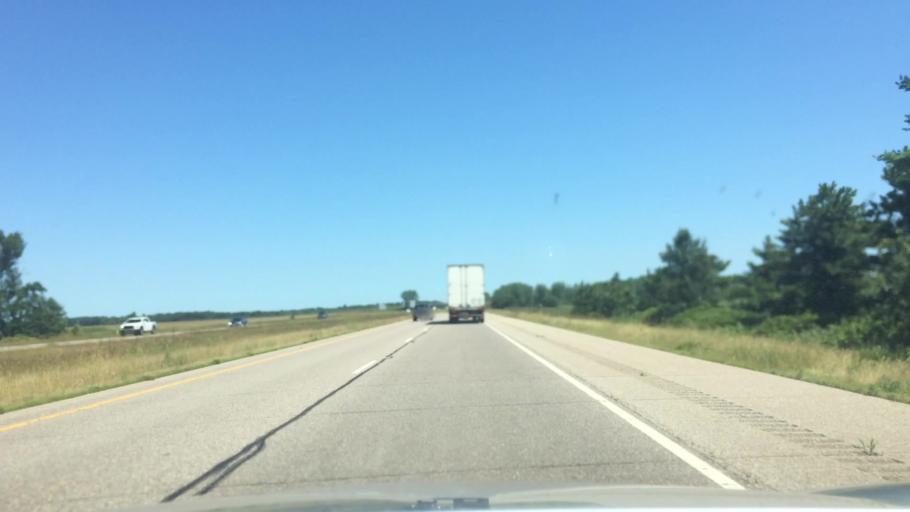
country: US
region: Wisconsin
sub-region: Waushara County
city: Wautoma
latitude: 44.1473
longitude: -89.5322
